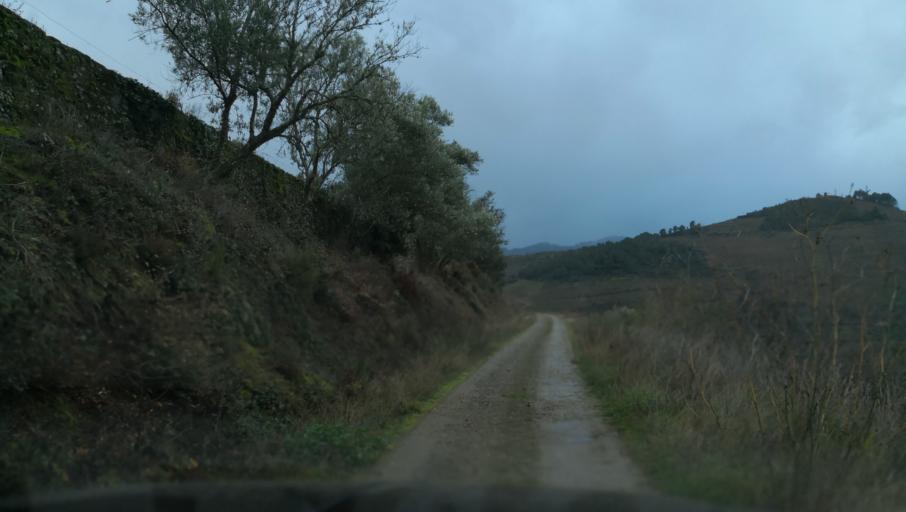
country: PT
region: Vila Real
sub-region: Vila Real
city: Vila Real
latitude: 41.2440
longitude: -7.7483
